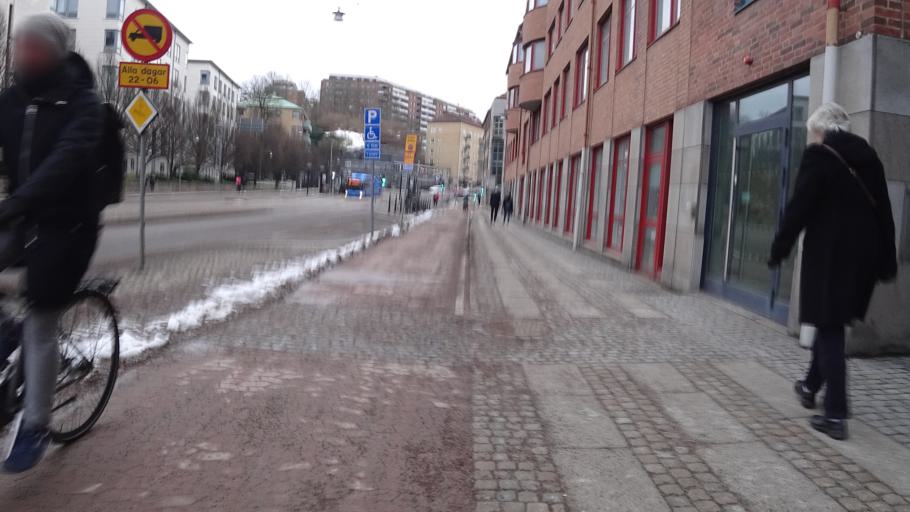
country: SE
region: Vaestra Goetaland
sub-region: Goteborg
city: Goeteborg
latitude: 57.6976
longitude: 11.9605
